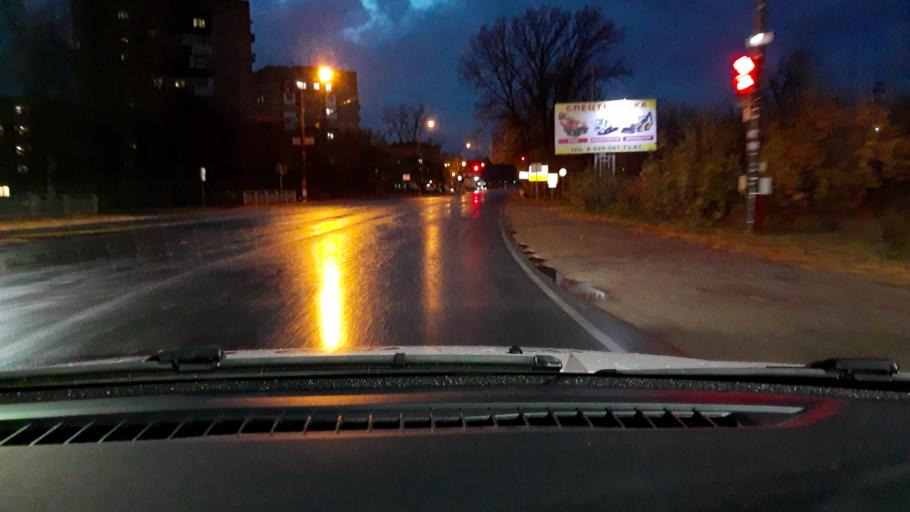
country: RU
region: Nizjnij Novgorod
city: Bor
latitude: 56.3537
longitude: 44.0753
